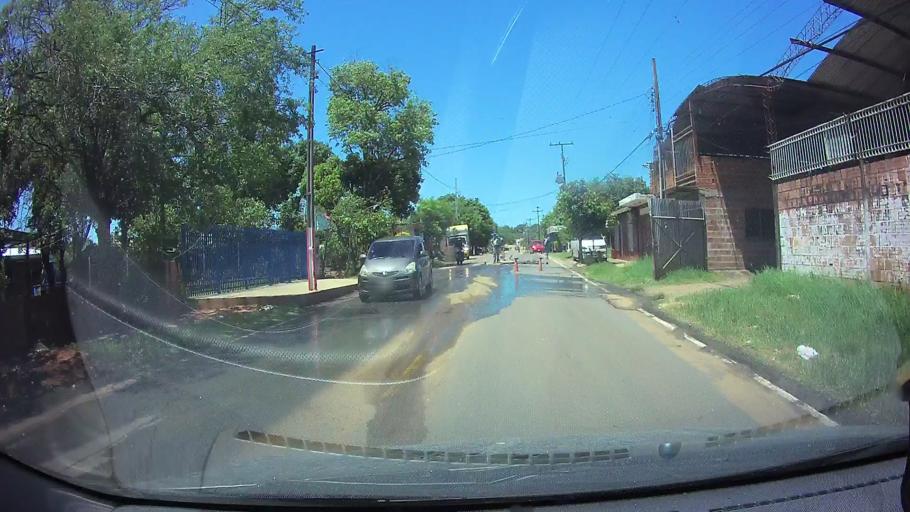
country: PY
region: Central
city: San Lorenzo
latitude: -25.3269
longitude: -57.4851
